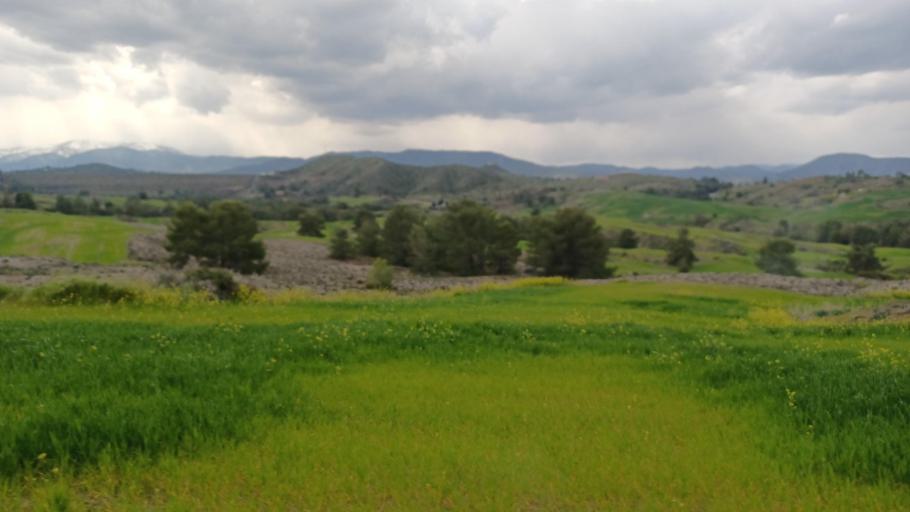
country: CY
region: Lefkosia
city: Lefka
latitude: 35.0807
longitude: 32.9078
